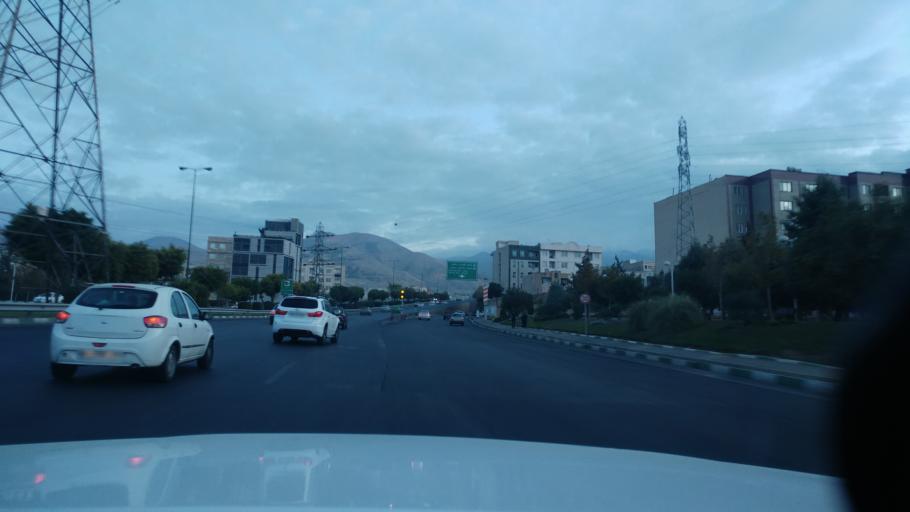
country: IR
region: Tehran
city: Tehran
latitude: 35.7474
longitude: 51.3147
